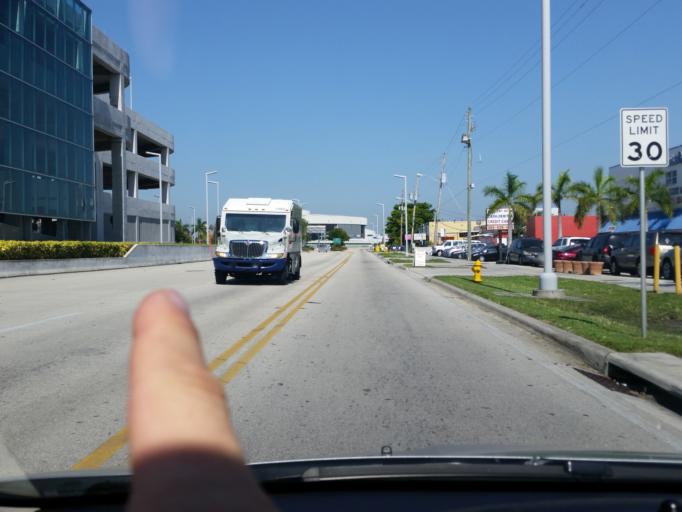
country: US
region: Florida
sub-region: Miami-Dade County
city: Brownsville
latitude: 25.7986
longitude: -80.2609
